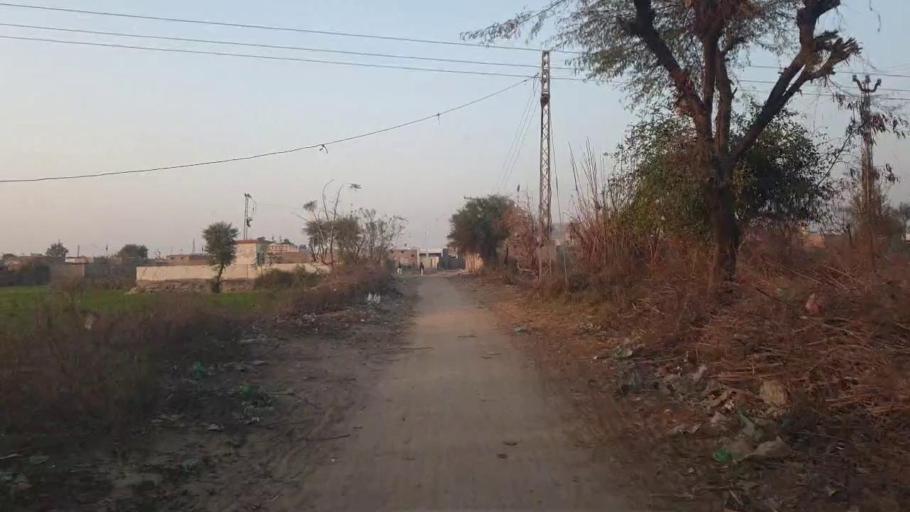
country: PK
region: Sindh
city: Bhit Shah
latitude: 25.8745
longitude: 68.5432
